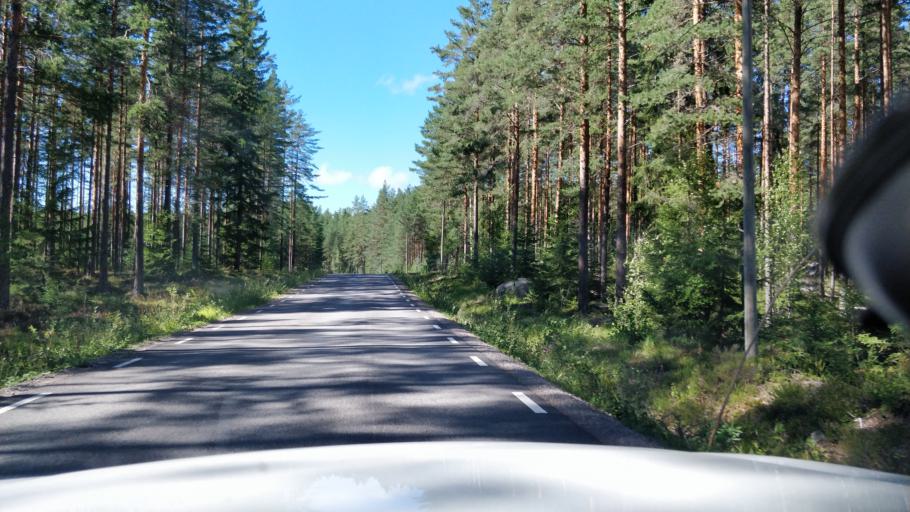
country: SE
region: Dalarna
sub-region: Faluns Kommun
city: Bjursas
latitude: 60.7510
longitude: 15.5248
